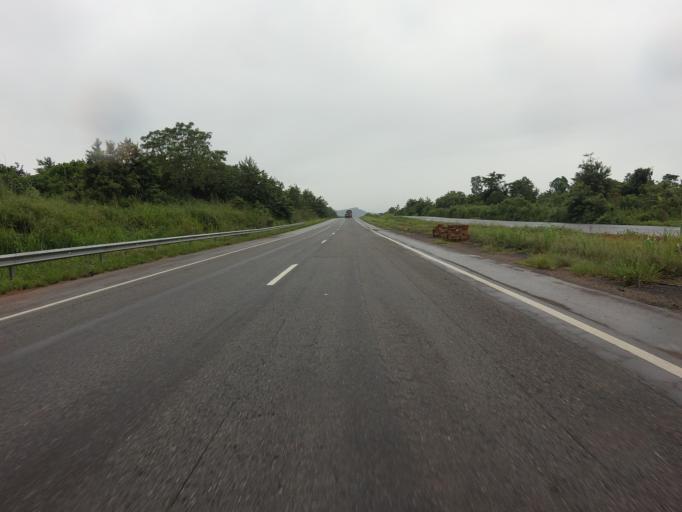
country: GH
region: Eastern
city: Suhum
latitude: 6.0822
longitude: -0.4743
